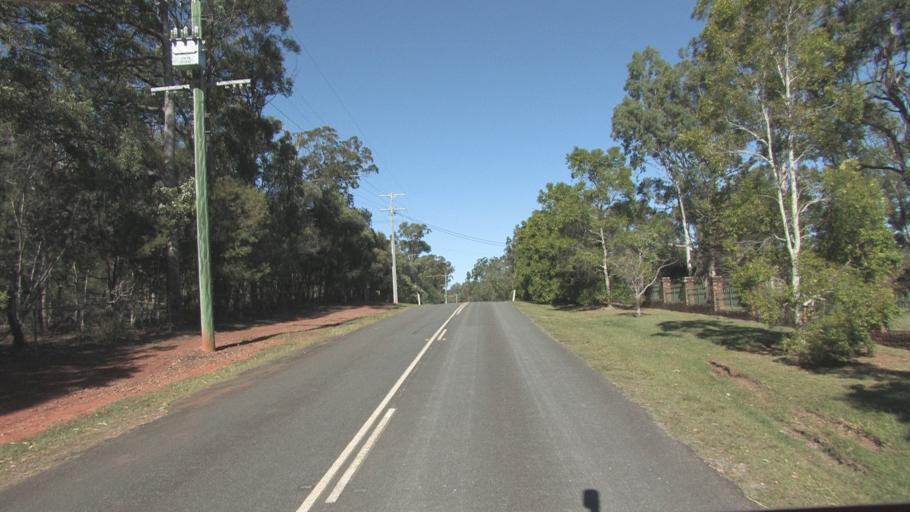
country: AU
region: Queensland
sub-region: Logan
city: Springwood
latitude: -27.5943
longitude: 153.1583
